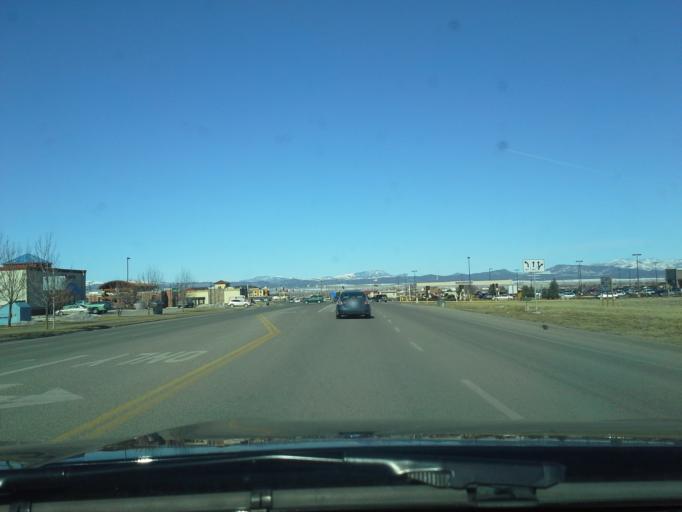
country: US
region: Montana
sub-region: Lewis and Clark County
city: Helena
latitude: 46.6133
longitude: -112.0048
